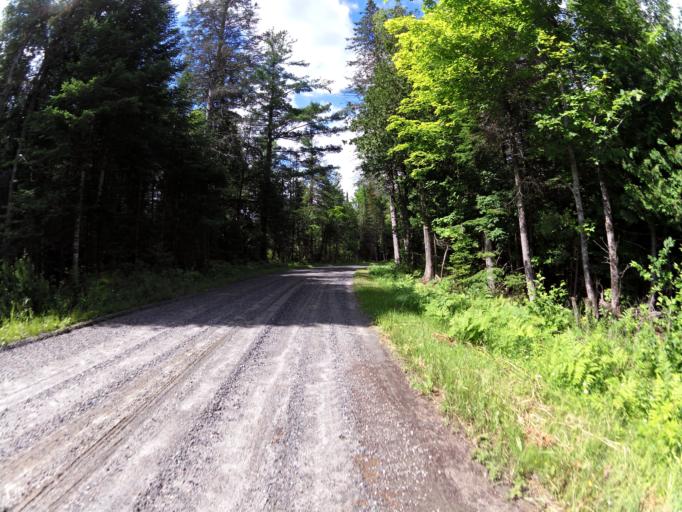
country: CA
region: Ontario
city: Perth
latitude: 45.0729
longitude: -76.4702
